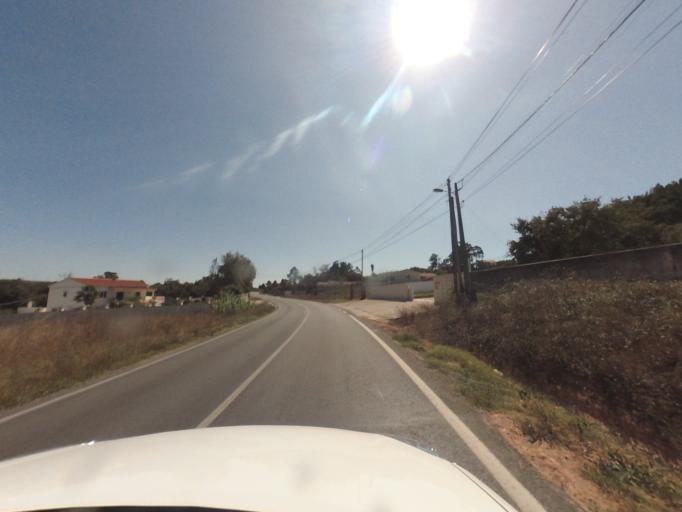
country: PT
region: Leiria
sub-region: Alcobaca
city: Turquel
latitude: 39.4444
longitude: -8.9768
